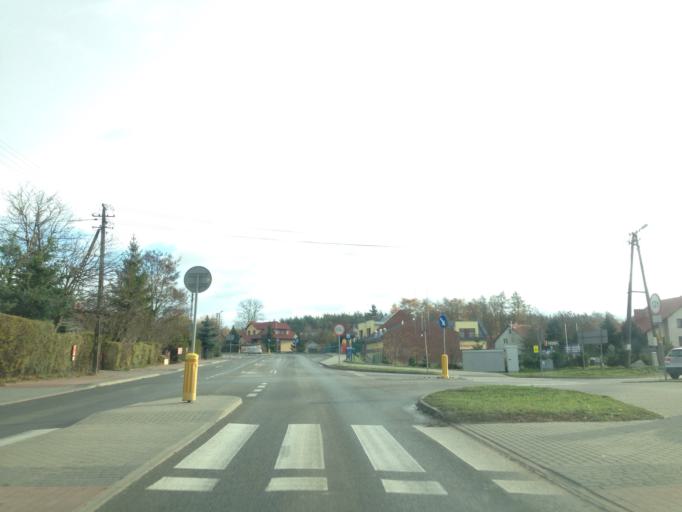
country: PL
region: Pomeranian Voivodeship
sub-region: Powiat gdanski
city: Lublewo Gdanskie
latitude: 54.2840
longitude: 18.5015
